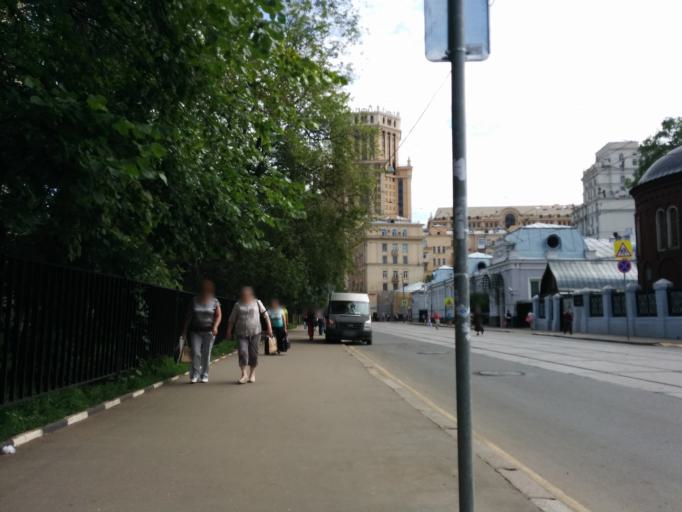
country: RU
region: Moscow
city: Zamoskvorech'ye
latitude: 55.7329
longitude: 37.6347
